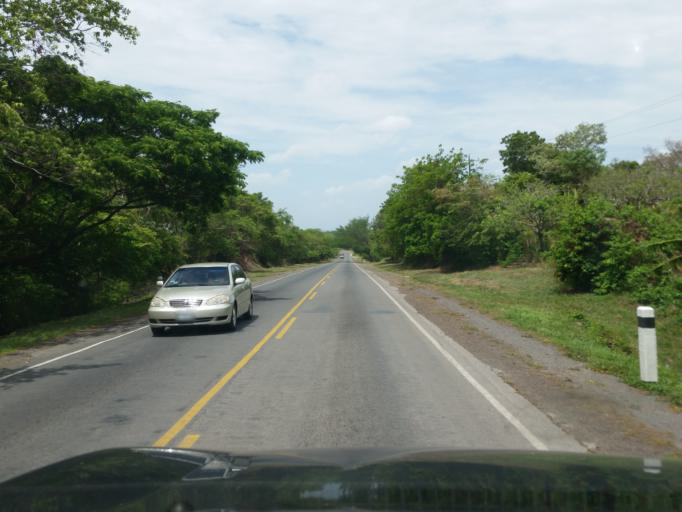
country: NI
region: Granada
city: Nandaime
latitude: 11.7983
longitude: -86.0468
